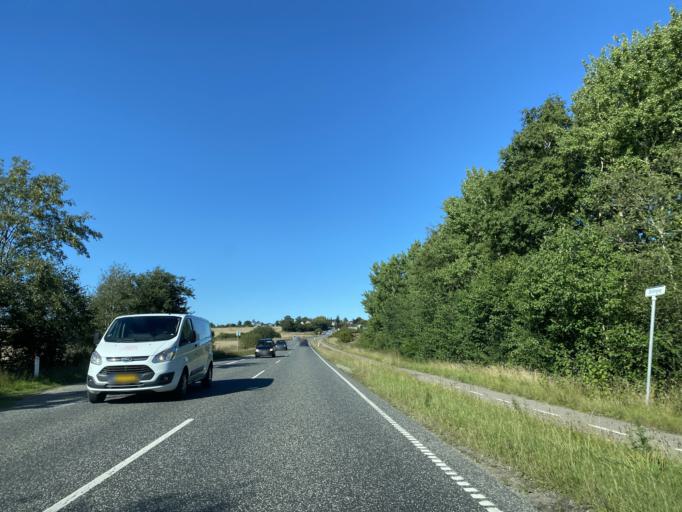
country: DK
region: Central Jutland
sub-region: Arhus Kommune
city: Sabro
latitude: 56.2050
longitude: 10.0178
